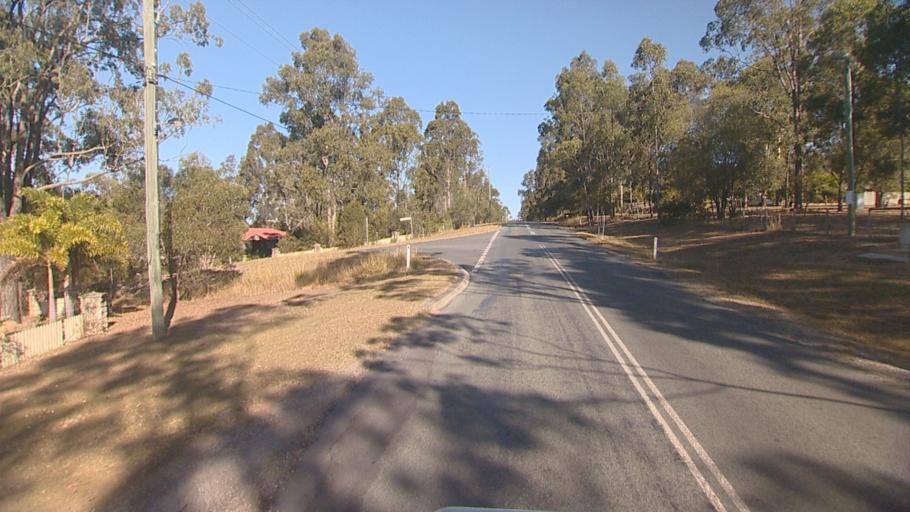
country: AU
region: Queensland
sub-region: Logan
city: Cedar Vale
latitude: -27.8557
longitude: 153.0378
